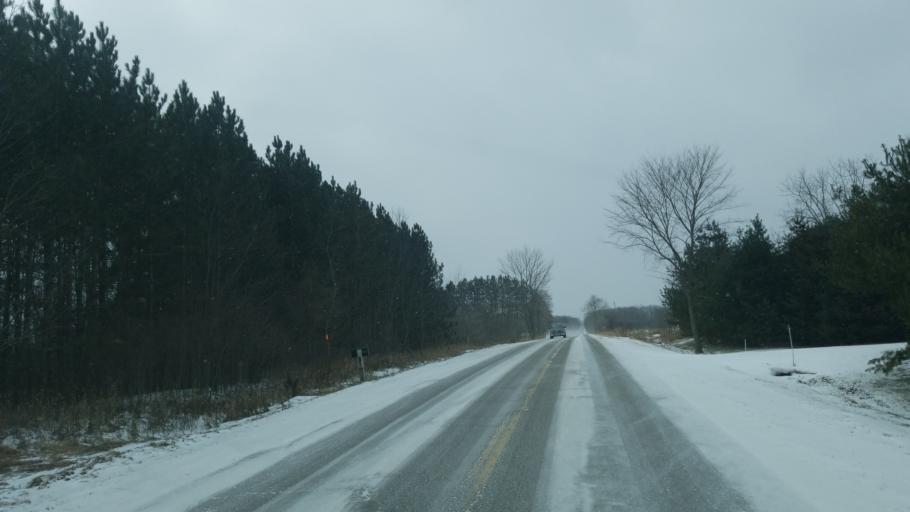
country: US
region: Michigan
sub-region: Osceola County
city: Evart
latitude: 44.0303
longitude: -85.2209
